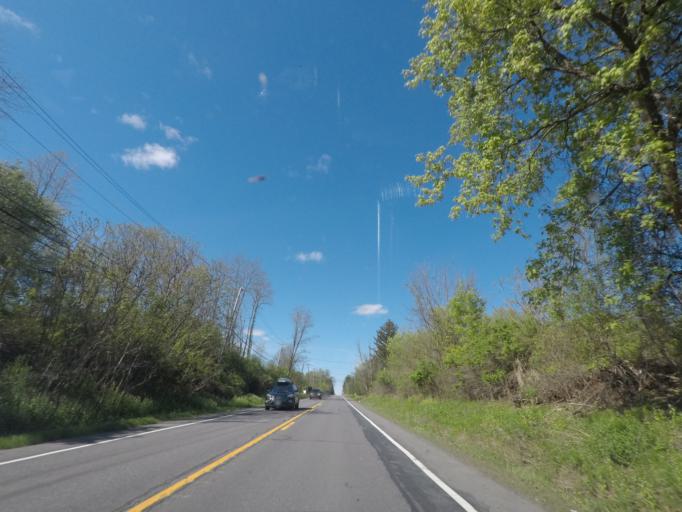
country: US
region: New York
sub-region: Albany County
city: Delmar
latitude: 42.5613
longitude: -73.8073
